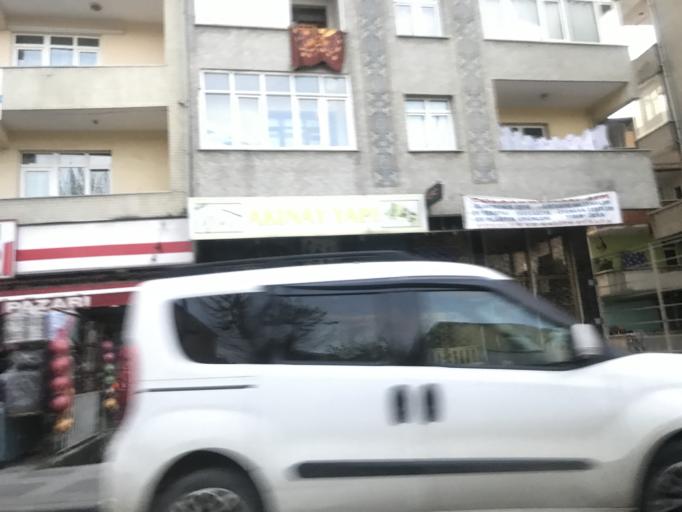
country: TR
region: Istanbul
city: Umraniye
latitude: 41.0374
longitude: 29.1015
